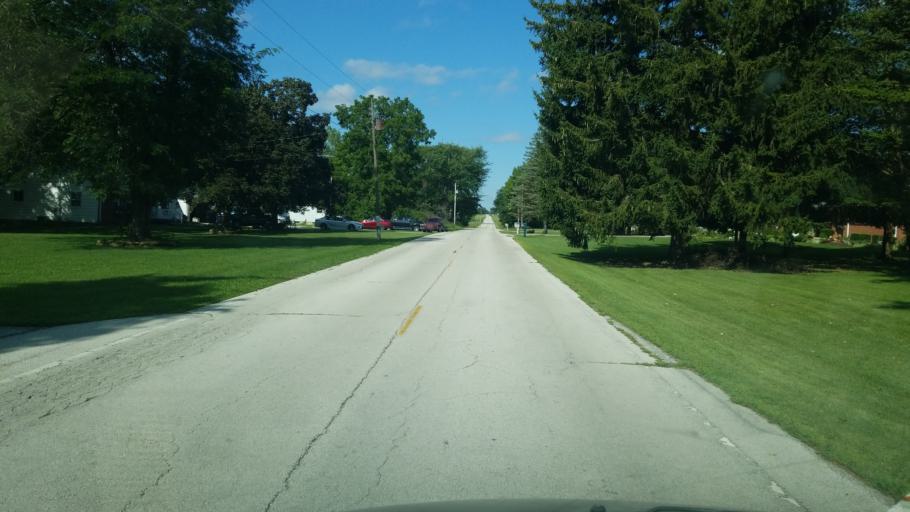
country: US
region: Ohio
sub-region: Seneca County
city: Fostoria
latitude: 41.1081
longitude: -83.4421
